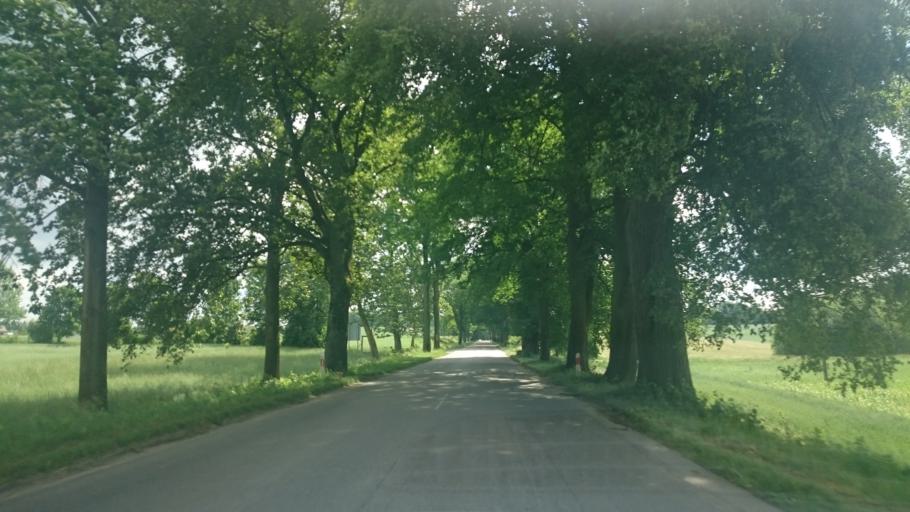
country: PL
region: Pomeranian Voivodeship
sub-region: Powiat starogardzki
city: Kaliska
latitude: 53.9678
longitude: 18.2557
